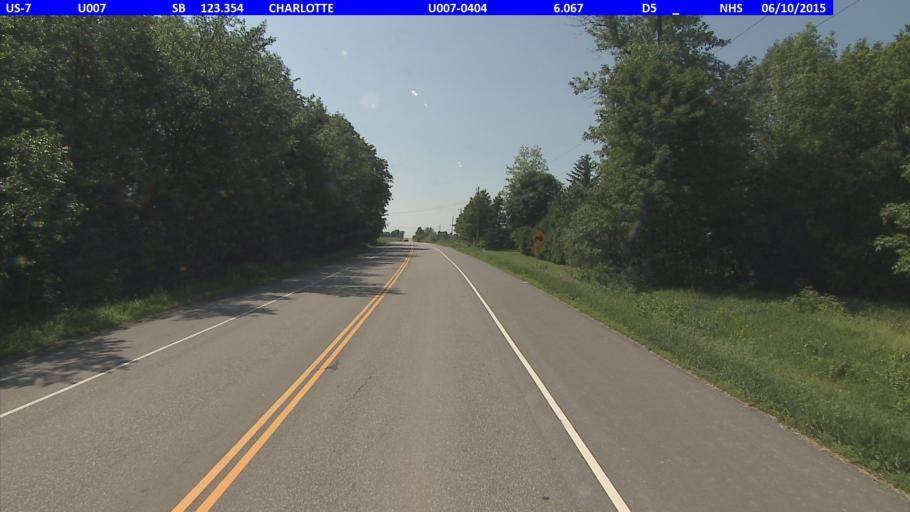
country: US
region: Vermont
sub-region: Chittenden County
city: Hinesburg
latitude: 44.3466
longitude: -73.2396
